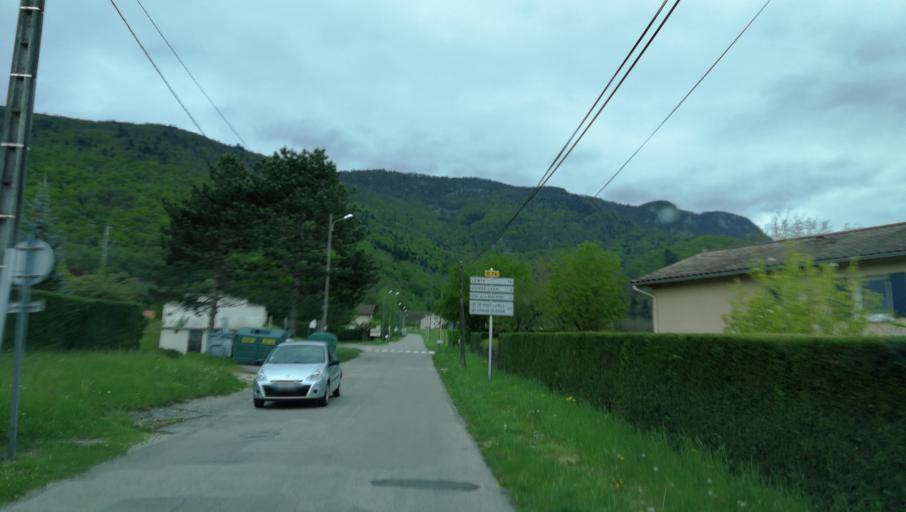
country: FR
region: Rhone-Alpes
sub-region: Departement de la Drome
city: Saint-Jean-en-Royans
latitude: 45.0096
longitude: 5.2912
